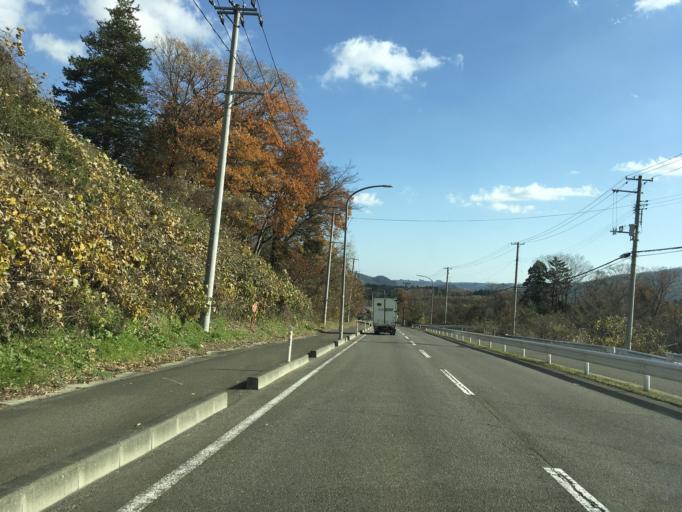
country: JP
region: Miyagi
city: Sendai
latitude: 38.2855
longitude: 140.7533
